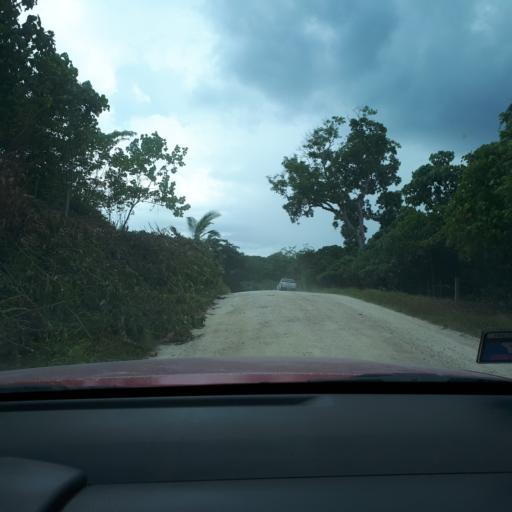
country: VU
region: Sanma
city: Luganville
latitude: -15.5781
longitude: 167.0304
